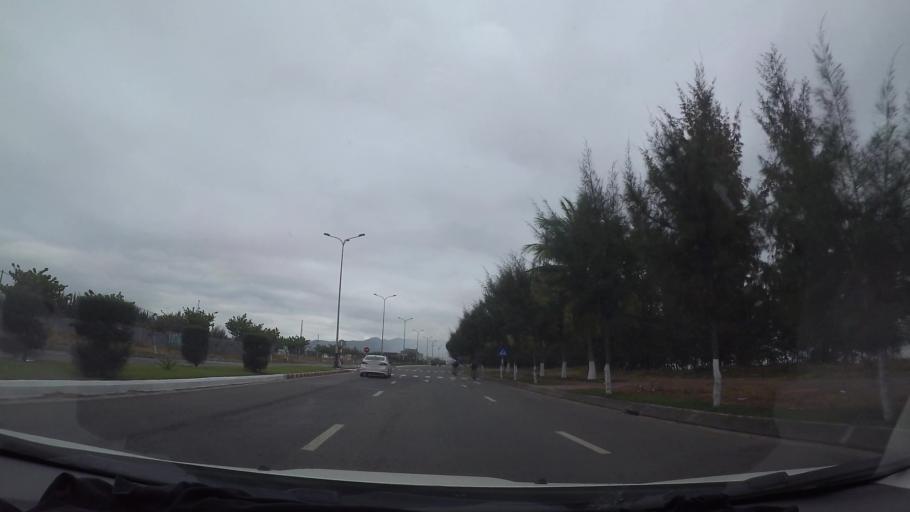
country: VN
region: Da Nang
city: Lien Chieu
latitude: 16.0976
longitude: 108.1433
